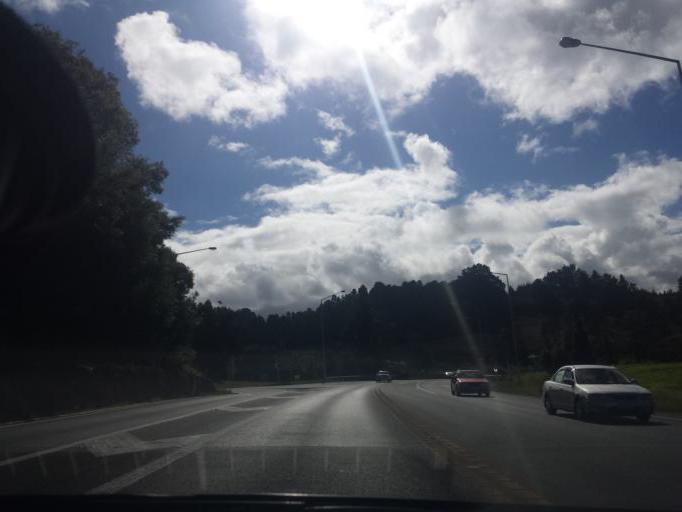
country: NZ
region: Auckland
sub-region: Auckland
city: Warkworth
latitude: -36.5167
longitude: 174.6697
